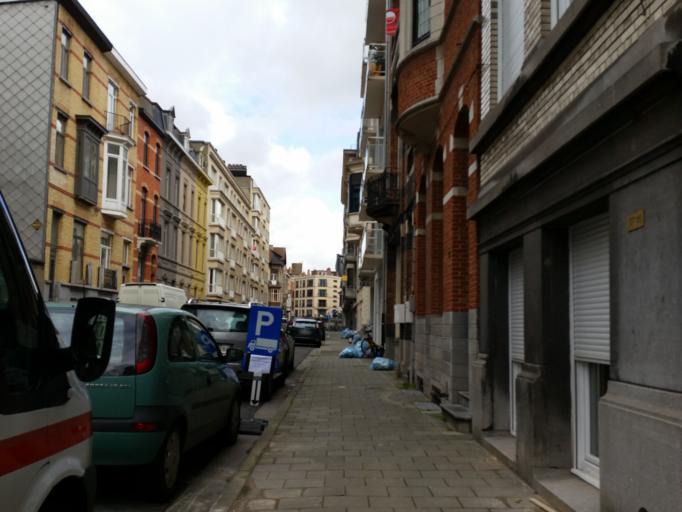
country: BE
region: Flanders
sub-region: Provincie Oost-Vlaanderen
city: Gent
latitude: 51.0352
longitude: 3.7151
